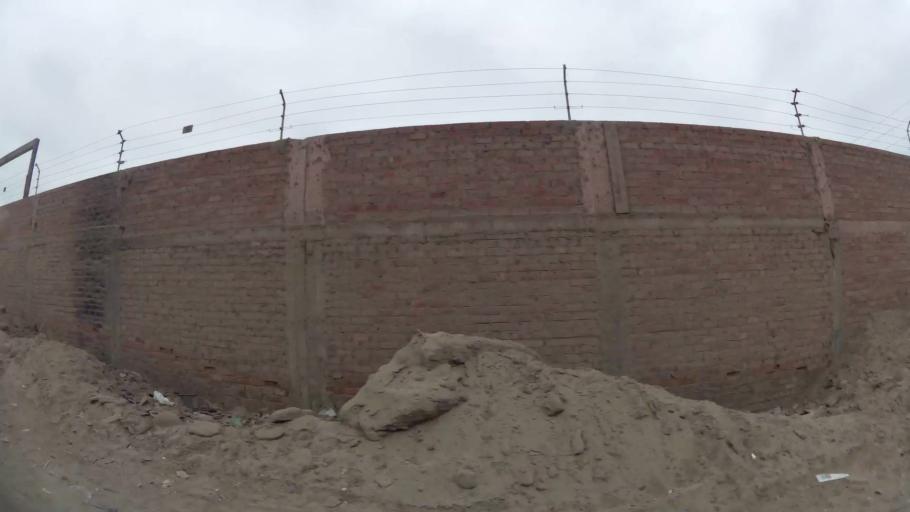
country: PE
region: Lima
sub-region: Lima
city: Surco
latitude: -12.2125
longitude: -76.9682
